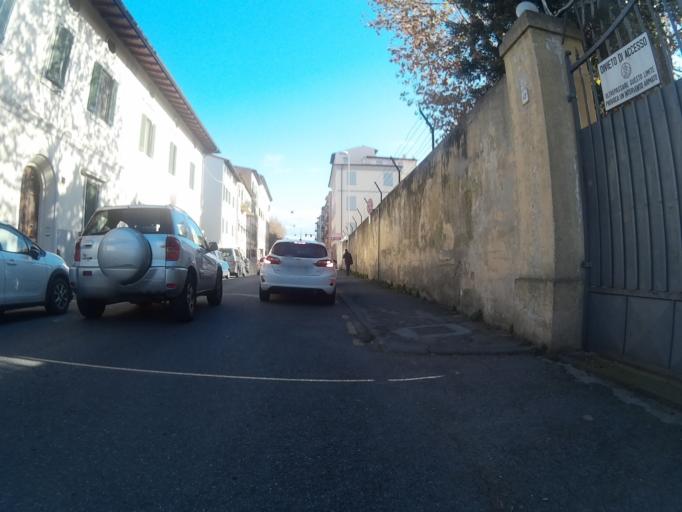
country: IT
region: Tuscany
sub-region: Provincia di Livorno
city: Livorno
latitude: 43.5498
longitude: 10.3208
